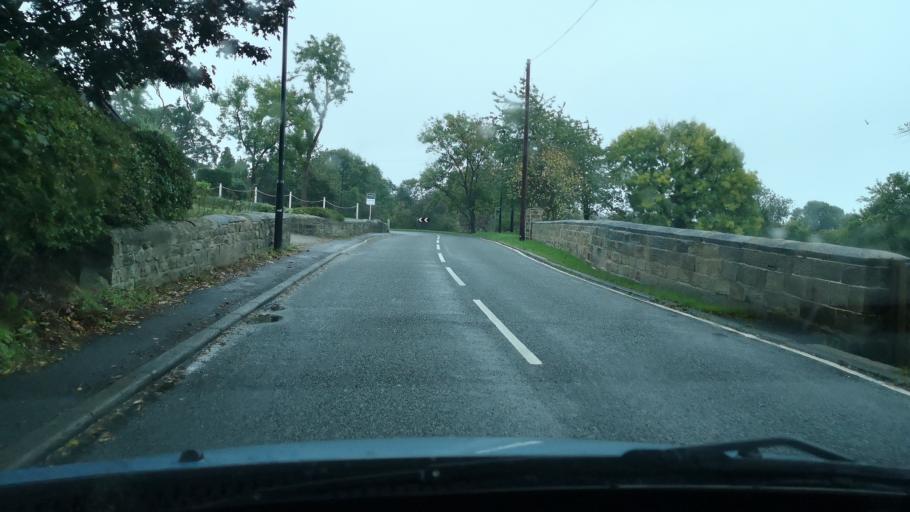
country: GB
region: England
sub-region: City and Borough of Wakefield
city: Low Ackworth
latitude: 53.6572
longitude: -1.3376
